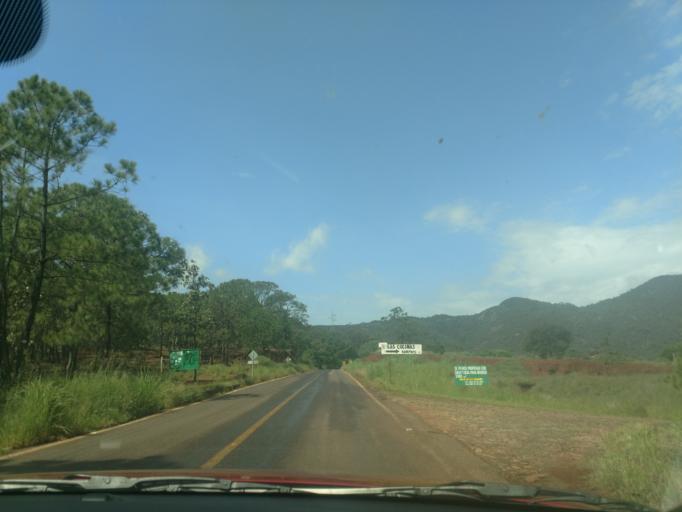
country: MX
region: Jalisco
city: Talpa de Allende
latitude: 20.4337
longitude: -104.7870
